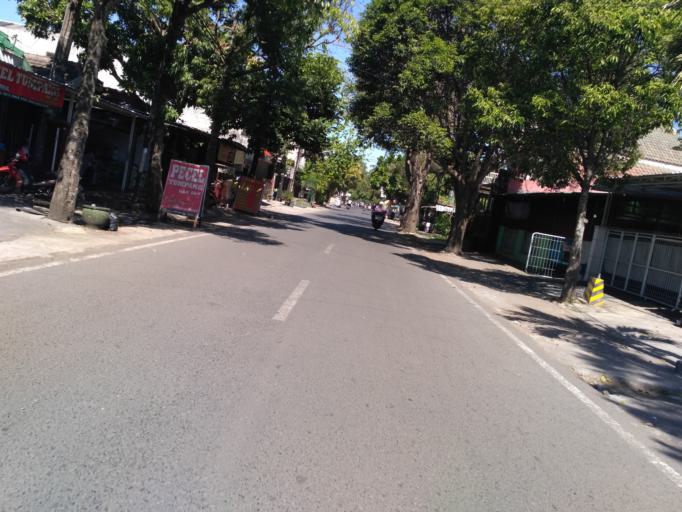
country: ID
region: East Java
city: Malang
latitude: -7.9746
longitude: 112.6659
